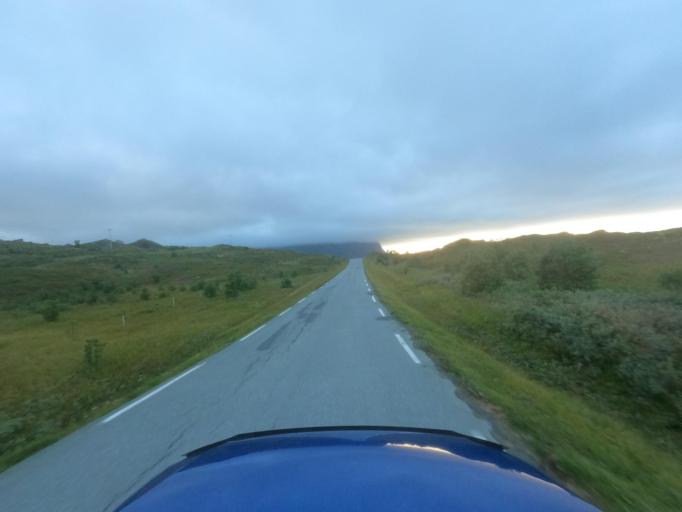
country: NO
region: Nordland
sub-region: Vestvagoy
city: Evjen
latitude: 68.2641
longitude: 13.7724
